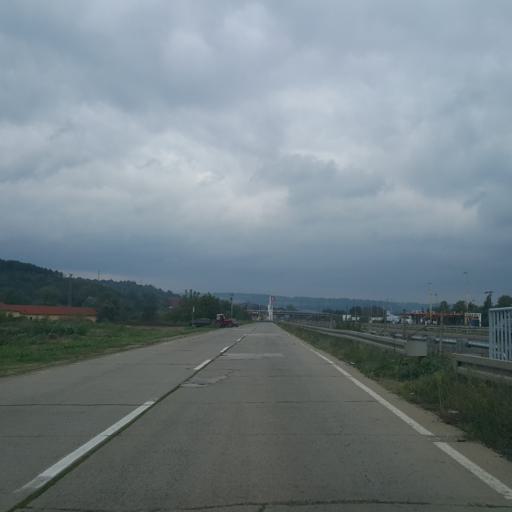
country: RS
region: Central Serbia
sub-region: Nisavski Okrug
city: Aleksinac
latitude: 43.5309
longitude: 21.7029
